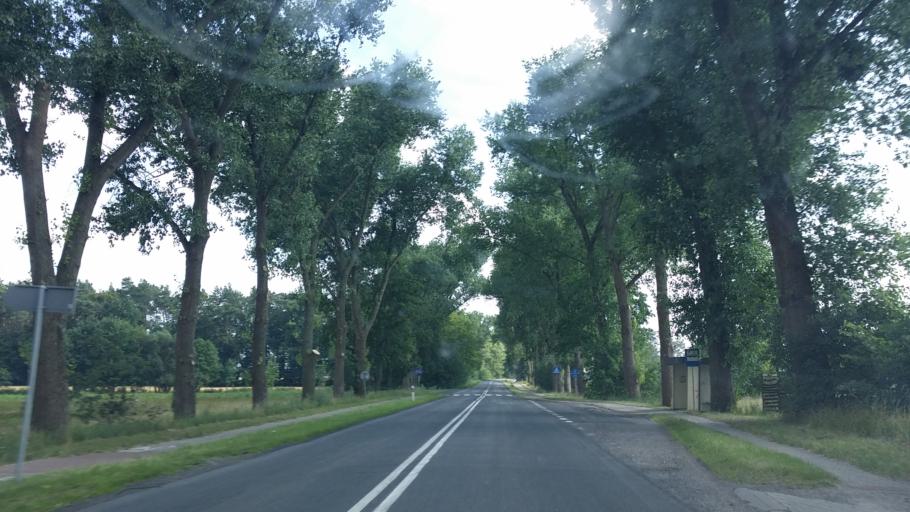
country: PL
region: Lubusz
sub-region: Powiat gorzowski
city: Klodawa
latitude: 52.8039
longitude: 15.2181
